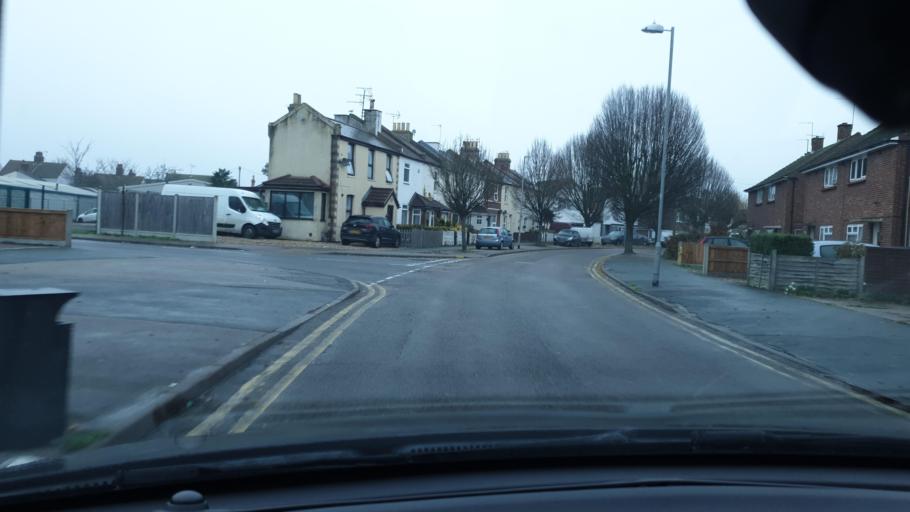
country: GB
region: England
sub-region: Essex
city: Clacton-on-Sea
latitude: 51.7923
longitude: 1.1435
